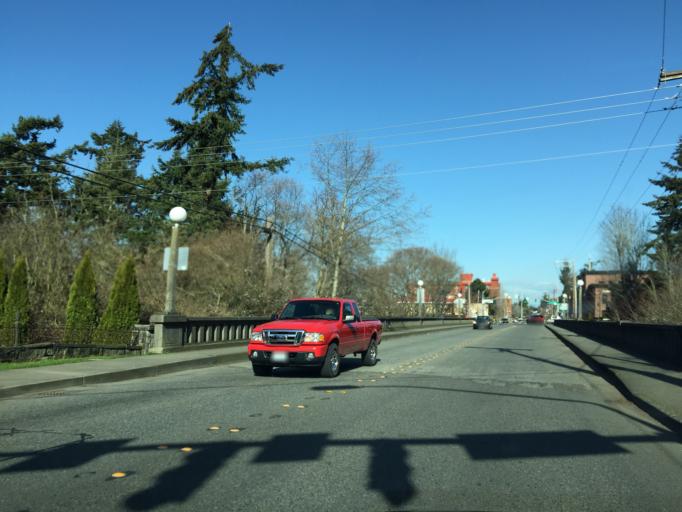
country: US
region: Washington
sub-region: Whatcom County
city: Bellingham
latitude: 48.7161
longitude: -122.5022
